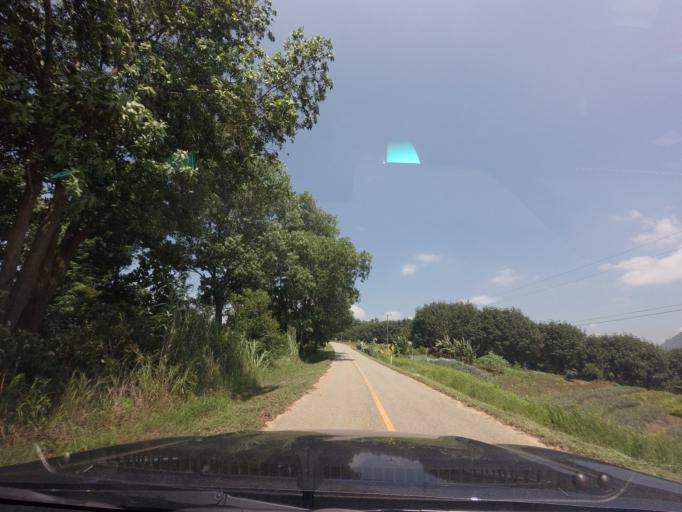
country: TH
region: Loei
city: Na Haeo
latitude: 17.5899
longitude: 100.9089
